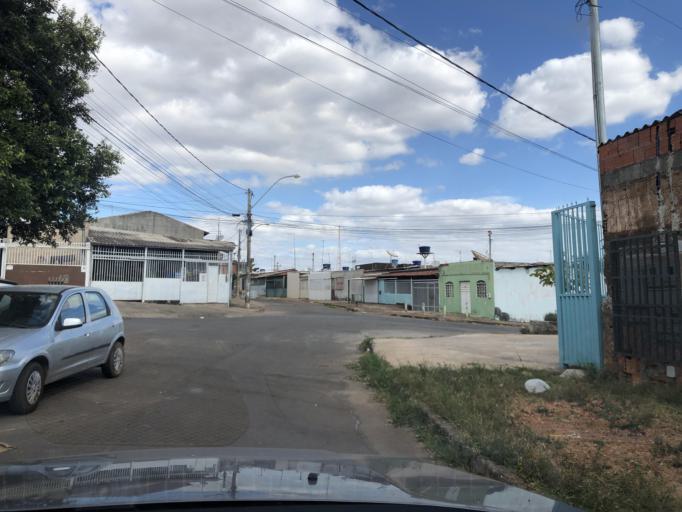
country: BR
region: Federal District
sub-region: Brasilia
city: Brasilia
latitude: -15.8855
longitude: -48.1291
